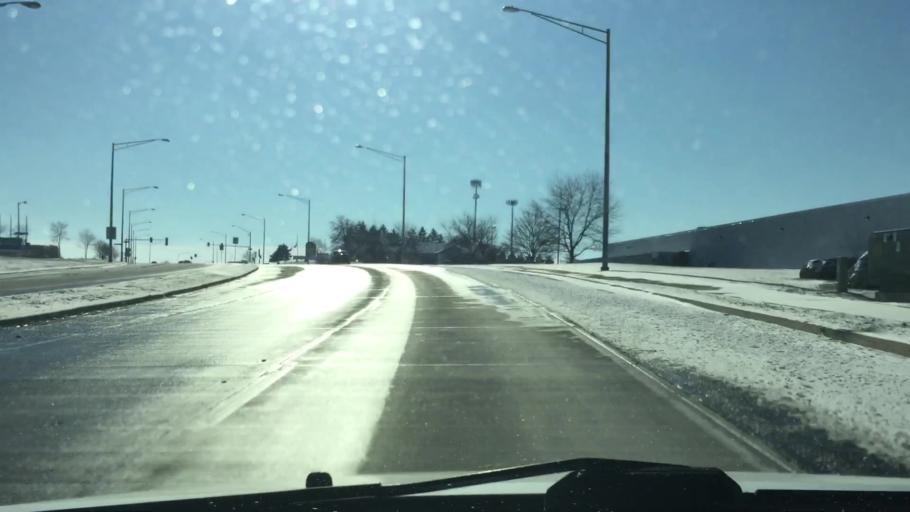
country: US
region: Illinois
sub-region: Kane County
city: Saint Charles
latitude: 41.9100
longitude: -88.2777
